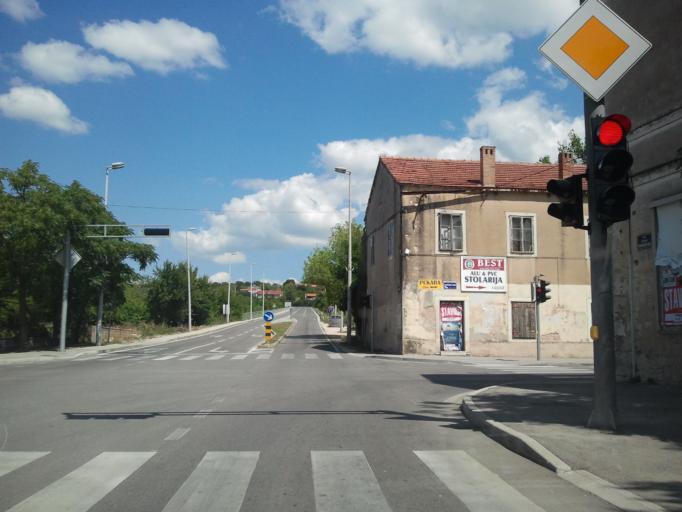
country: HR
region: Zadarska
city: Benkovac
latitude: 44.0334
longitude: 15.6167
